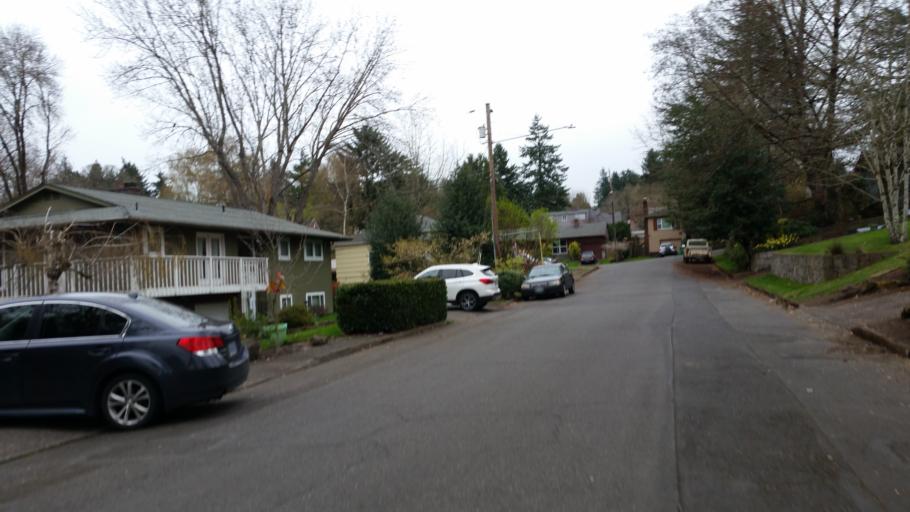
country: US
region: Oregon
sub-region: Washington County
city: Raleigh Hills
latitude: 45.4798
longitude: -122.7264
